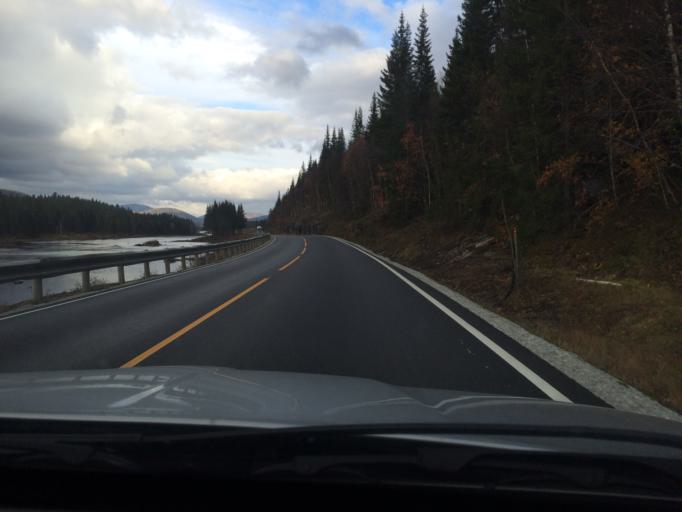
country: NO
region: Nord-Trondelag
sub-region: Namsskogan
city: Namsskogan
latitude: 64.7899
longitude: 12.9124
